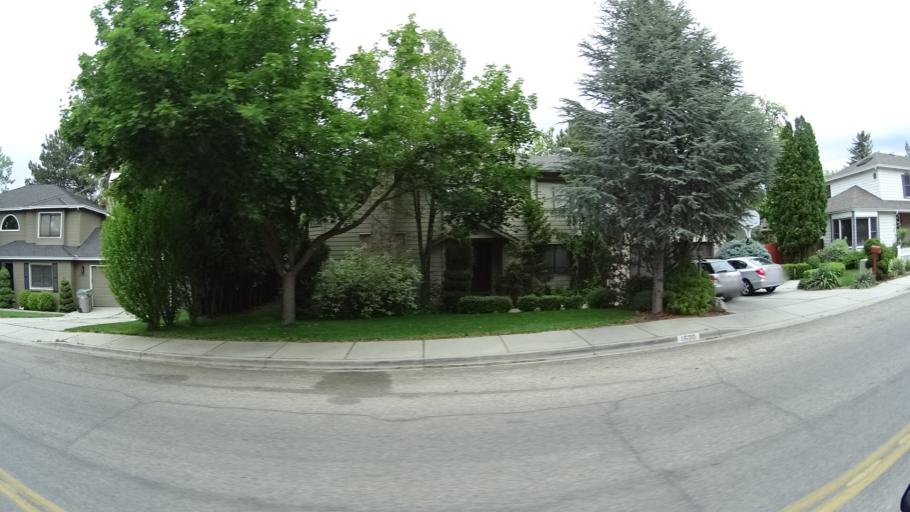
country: US
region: Idaho
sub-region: Ada County
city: Boise
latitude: 43.6172
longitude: -116.1719
